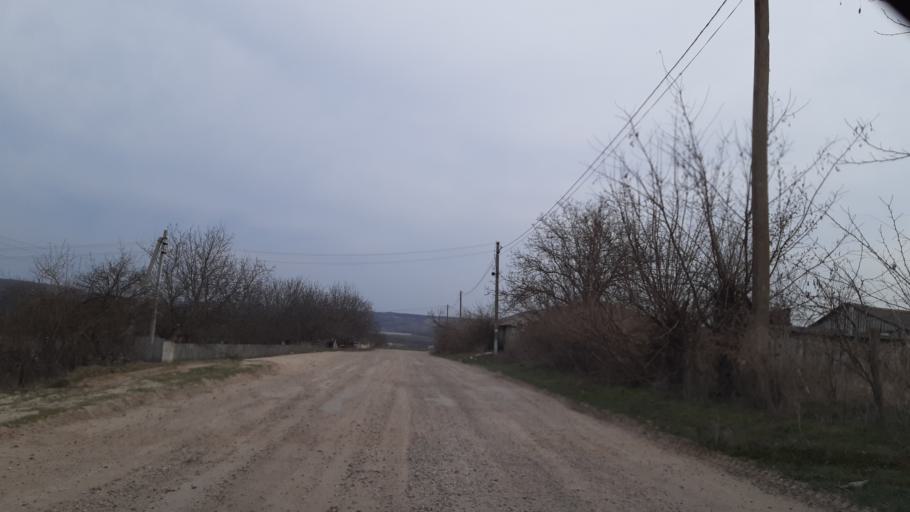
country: MD
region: Soldanesti
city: Soldanesti
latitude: 47.7102
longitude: 28.7080
